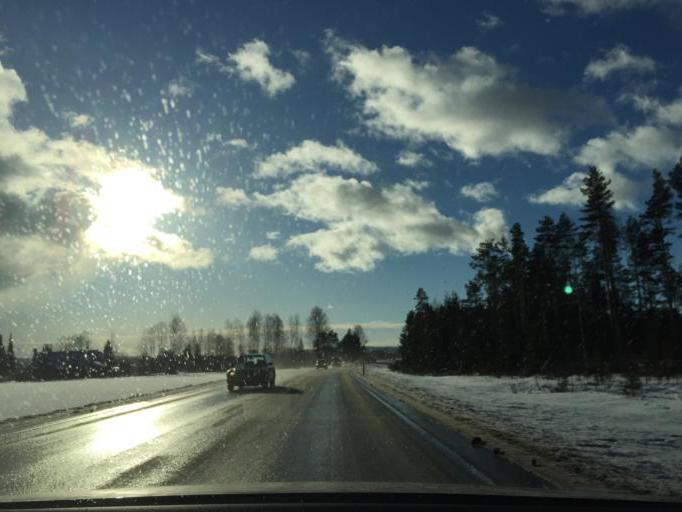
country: NO
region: Hedmark
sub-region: Sor-Odal
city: Skarnes
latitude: 60.2320
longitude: 11.6671
